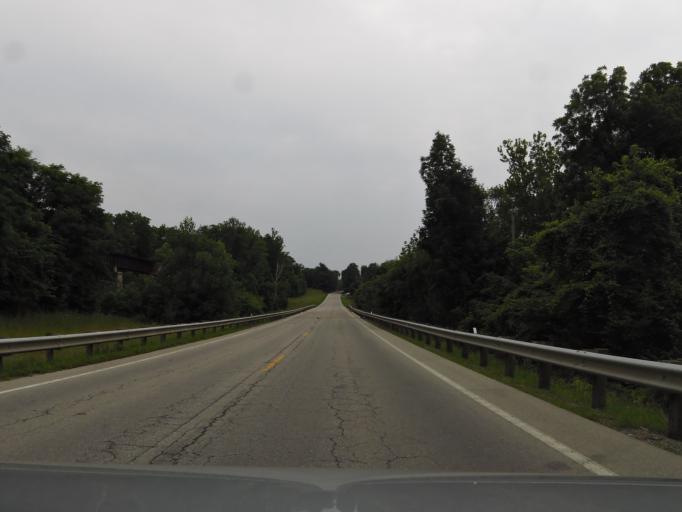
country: US
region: Ohio
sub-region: Clinton County
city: Wilmington
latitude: 39.3847
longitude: -83.8598
